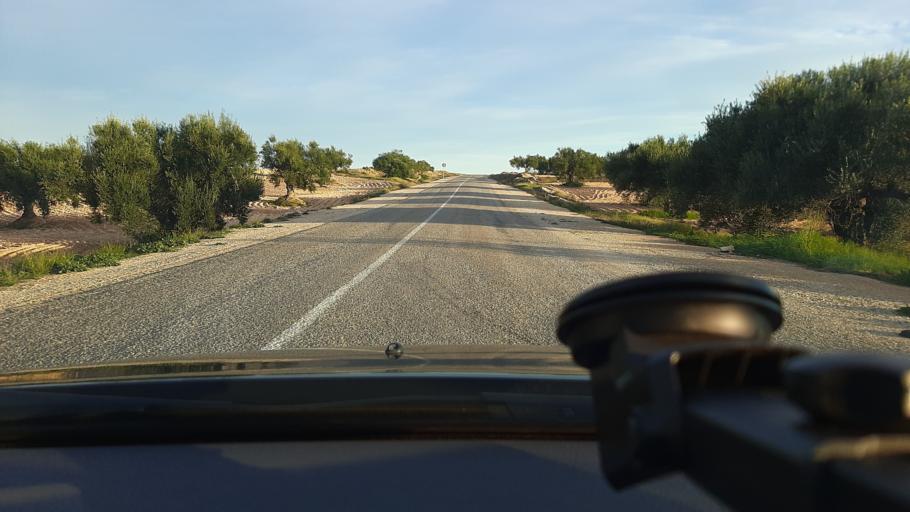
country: TN
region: Safaqis
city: Sfax
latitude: 34.9559
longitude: 10.5456
